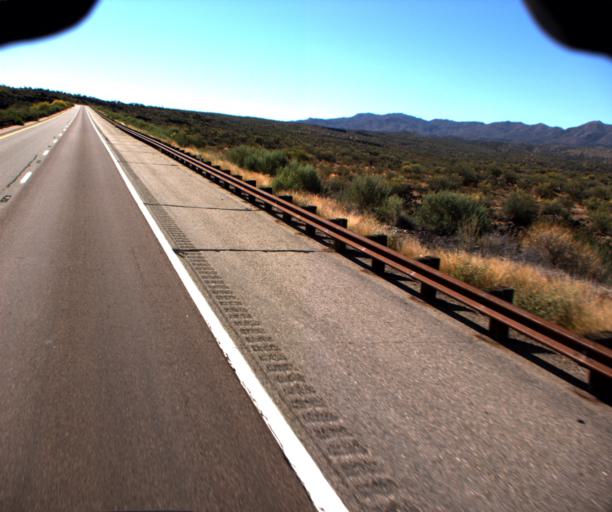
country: US
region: Arizona
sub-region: Yavapai County
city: Bagdad
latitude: 34.5065
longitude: -113.4122
